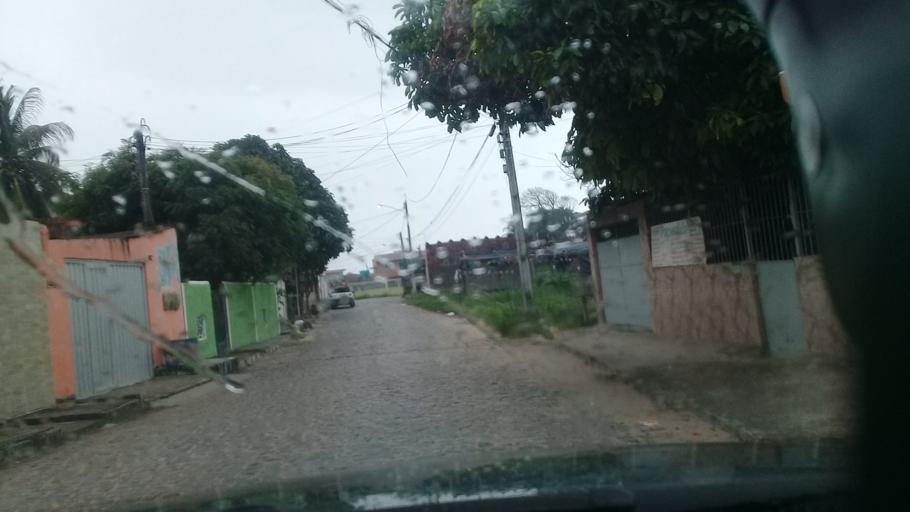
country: BR
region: Pernambuco
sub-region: Itamaraca
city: Itamaraca
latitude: -7.7444
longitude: -34.8271
